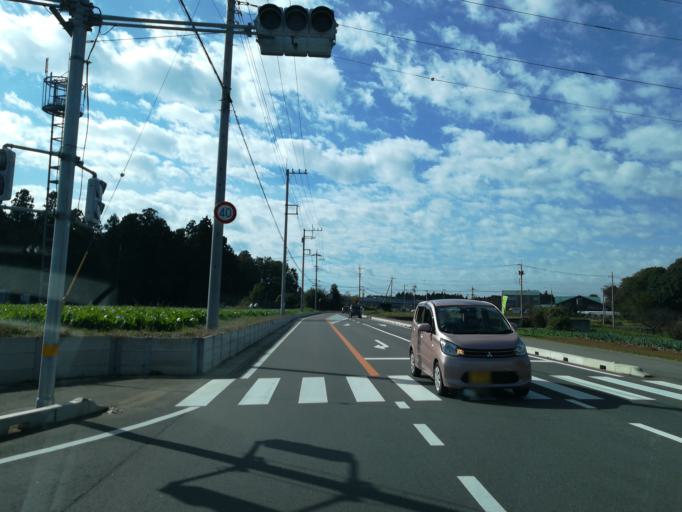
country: JP
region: Ibaraki
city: Naka
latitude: 36.0606
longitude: 140.0864
